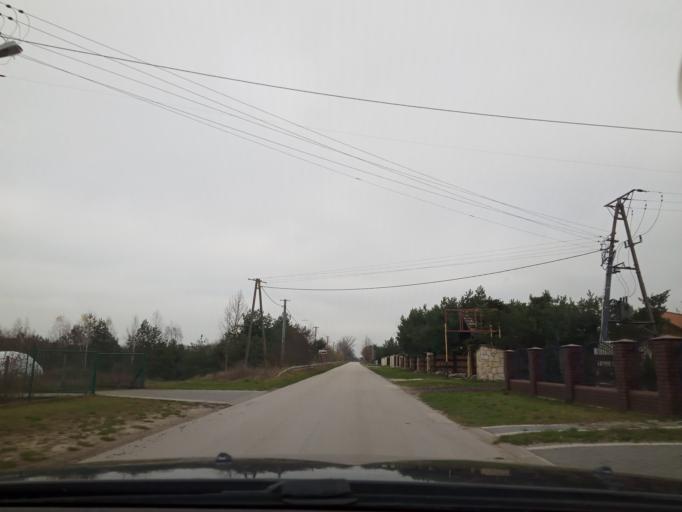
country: PL
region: Swietokrzyskie
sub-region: Powiat jedrzejowski
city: Imielno
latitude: 50.5904
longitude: 20.4773
